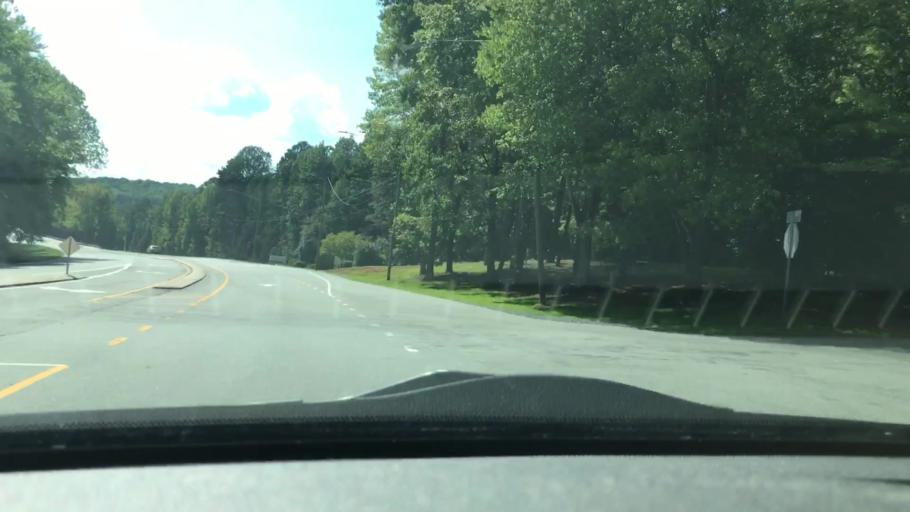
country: US
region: North Carolina
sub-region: Randolph County
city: Asheboro
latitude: 35.7354
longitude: -79.8158
